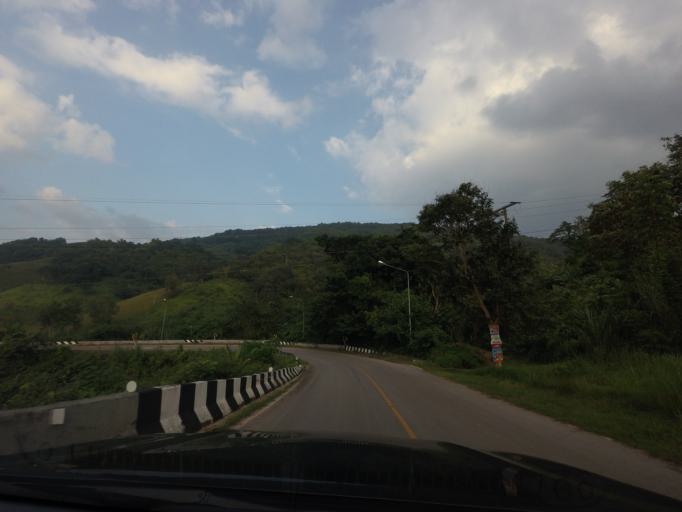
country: TH
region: Loei
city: Na Haeo
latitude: 17.3688
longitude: 101.0491
